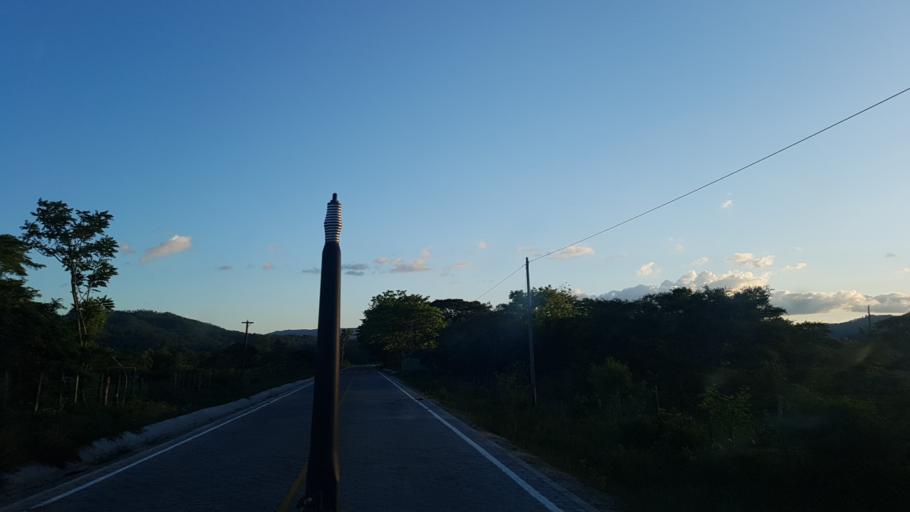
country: HN
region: El Paraiso
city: Santa Cruz
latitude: 13.7249
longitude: -86.6225
